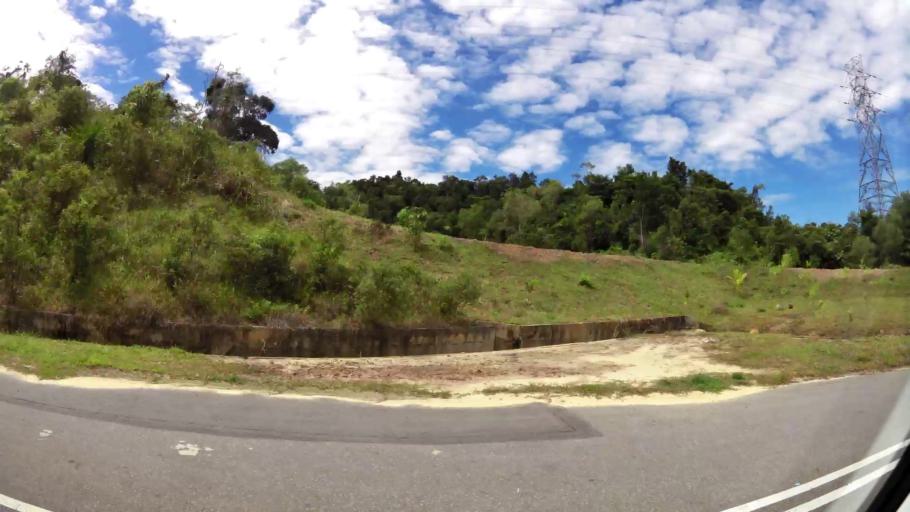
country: BN
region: Brunei and Muara
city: Bandar Seri Begawan
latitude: 4.9697
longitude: 115.0067
